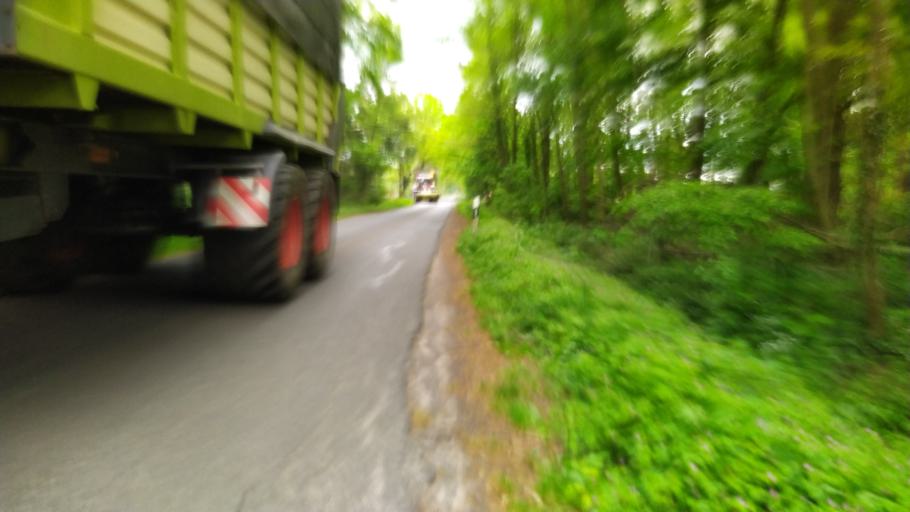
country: DE
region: Lower Saxony
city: Farven
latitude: 53.4032
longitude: 9.3589
